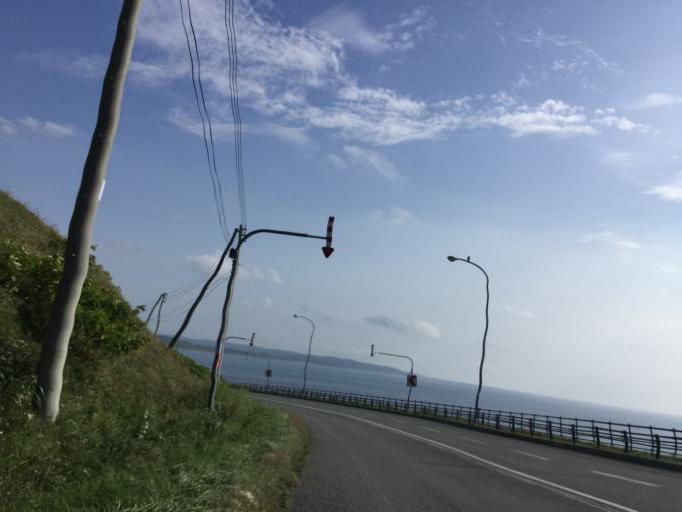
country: JP
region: Hokkaido
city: Wakkanai
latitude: 45.3798
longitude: 141.6538
